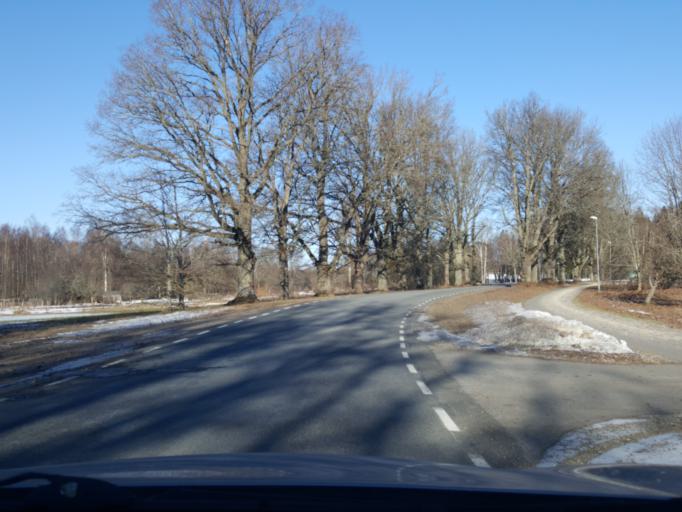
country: EE
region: Viljandimaa
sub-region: Vohma linn
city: Vohma
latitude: 58.5566
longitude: 25.5557
